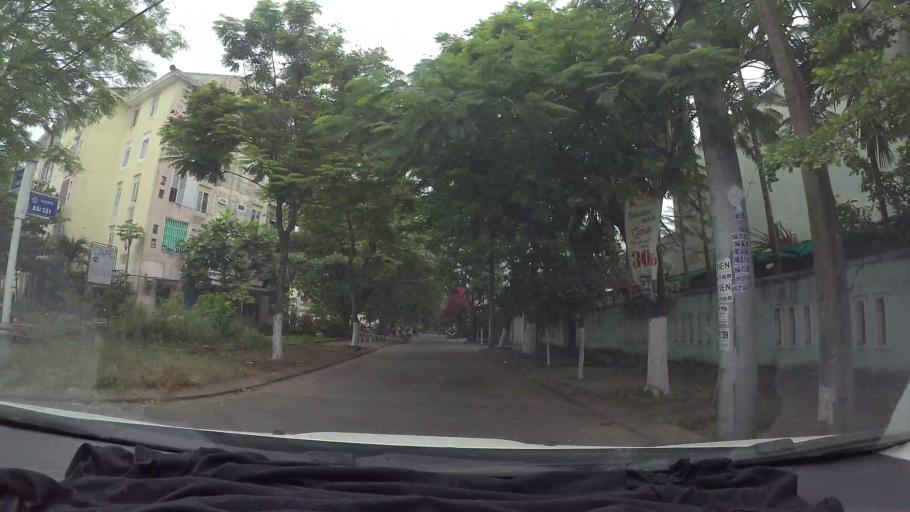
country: VN
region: Da Nang
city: Cam Le
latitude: 16.0289
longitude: 108.2123
